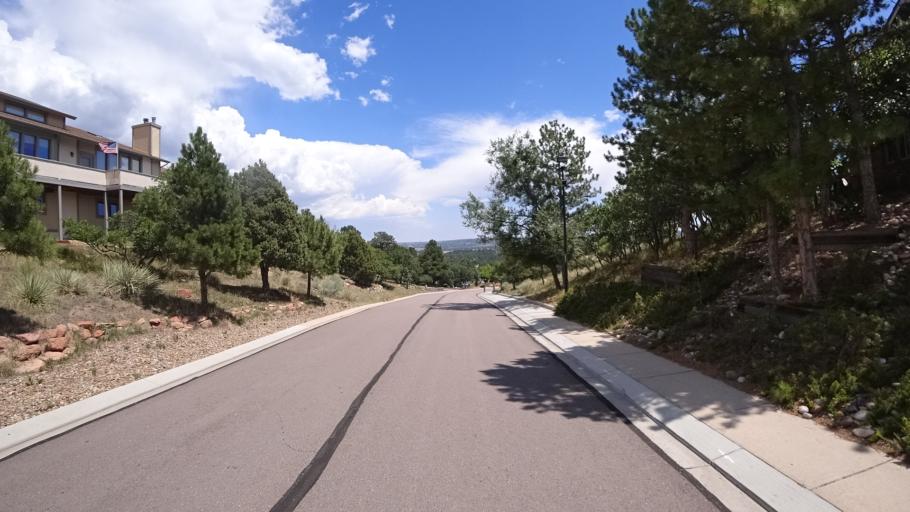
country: US
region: Colorado
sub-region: El Paso County
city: Air Force Academy
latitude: 38.9389
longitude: -104.8458
